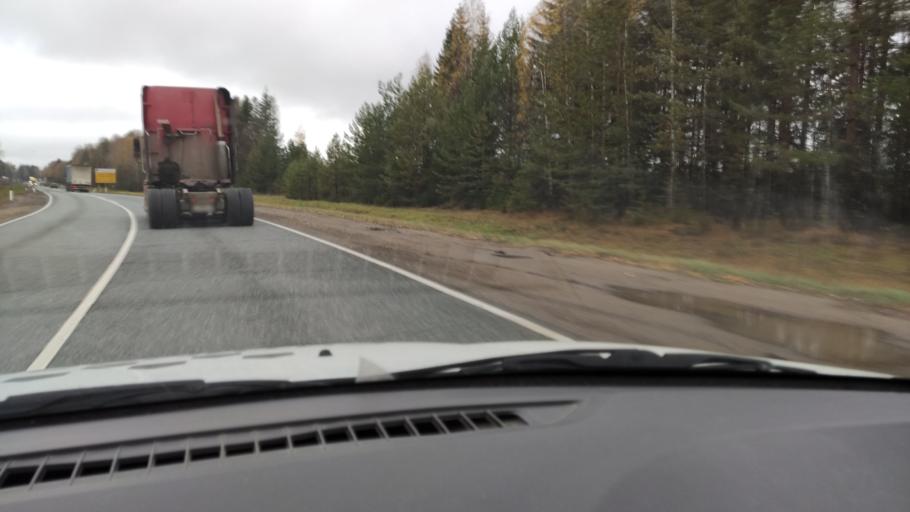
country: RU
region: Kirov
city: Belaya Kholunitsa
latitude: 58.8521
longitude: 50.7274
